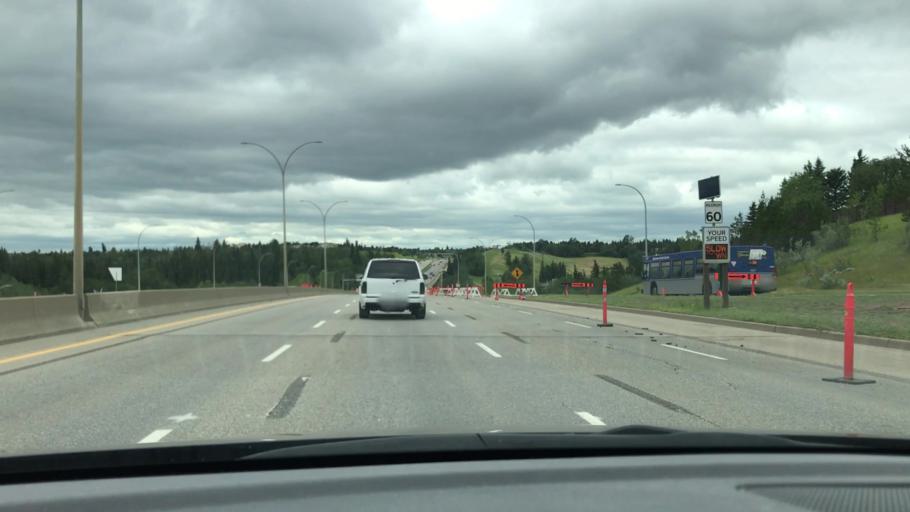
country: CA
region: Alberta
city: Edmonton
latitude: 53.4830
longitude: -113.5454
